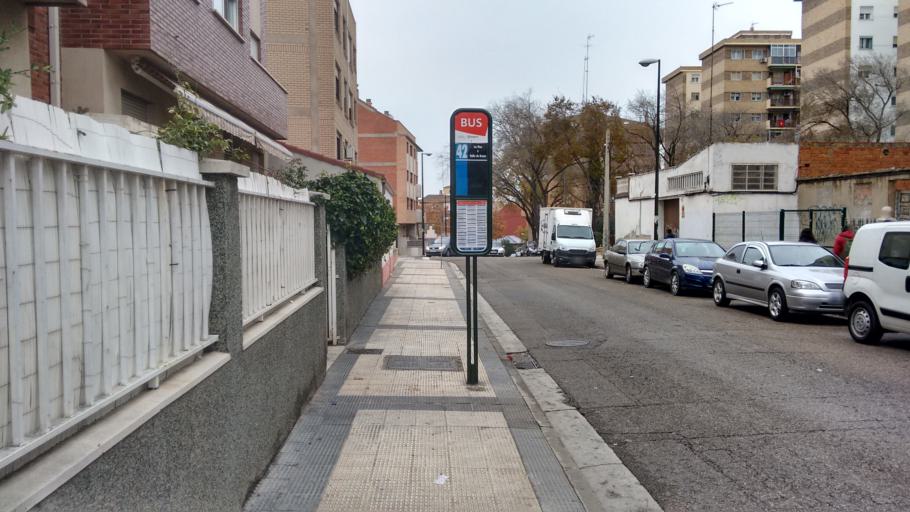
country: ES
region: Aragon
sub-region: Provincia de Zaragoza
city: Zaragoza
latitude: 41.6269
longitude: -0.8771
